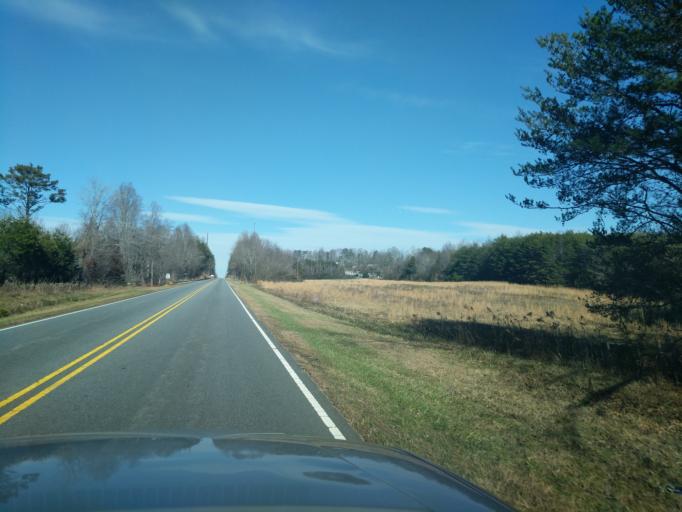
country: US
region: North Carolina
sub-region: Rutherford County
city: Rutherfordton
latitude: 35.4876
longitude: -81.9798
